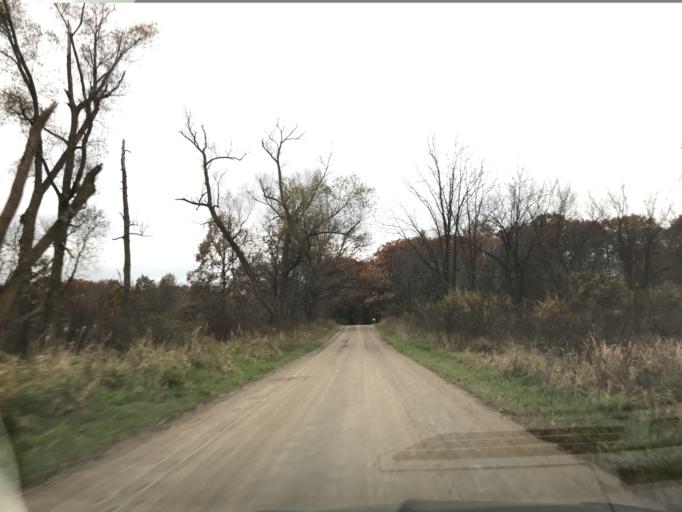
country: US
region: Michigan
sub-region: Lenawee County
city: Manitou Beach-Devils Lake
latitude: 42.0241
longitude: -84.3351
